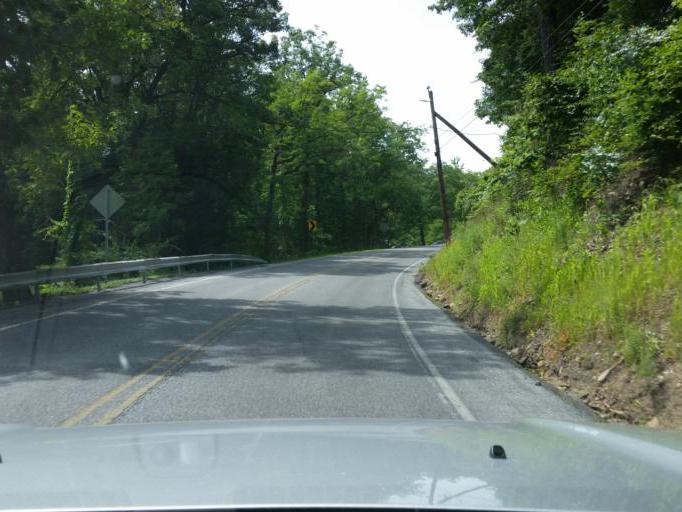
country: US
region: Pennsylvania
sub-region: Blair County
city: Altoona
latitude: 40.5559
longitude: -78.4459
